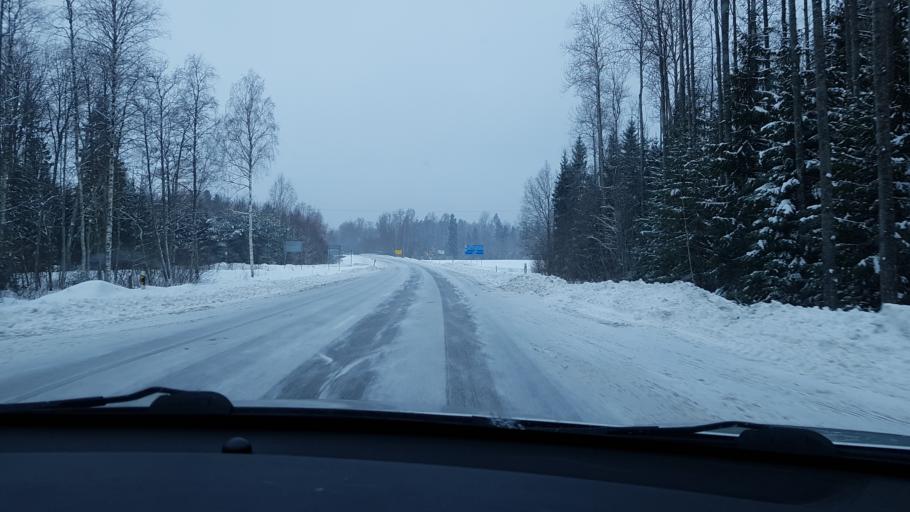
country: EE
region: Jaervamaa
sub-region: Tueri vald
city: Sarevere
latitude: 58.7178
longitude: 25.2751
